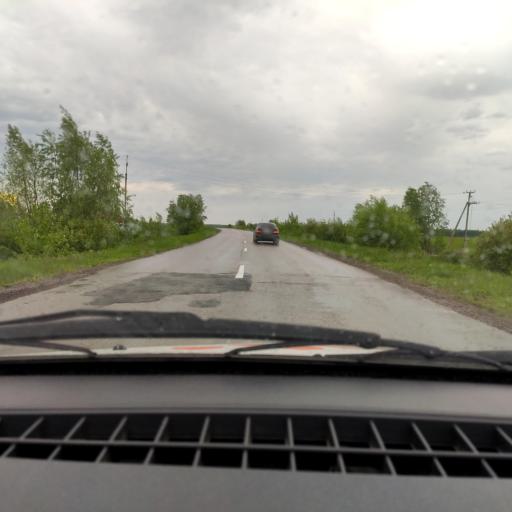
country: RU
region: Bashkortostan
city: Kudeyevskiy
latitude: 54.8429
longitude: 56.7957
